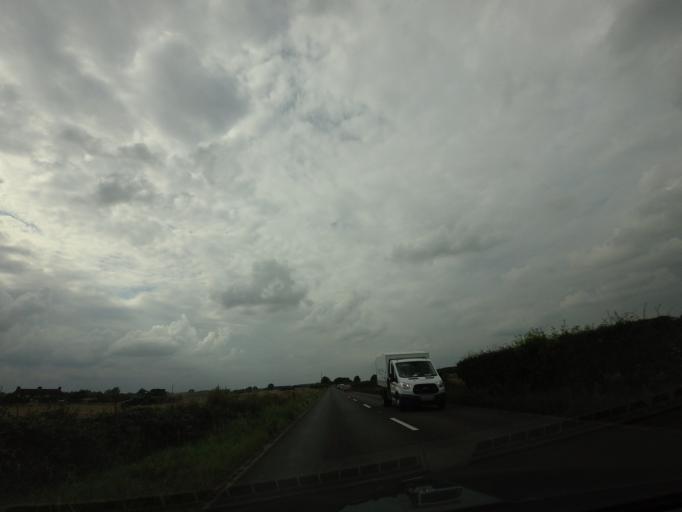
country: GB
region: England
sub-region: Shropshire
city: Tong
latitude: 52.6900
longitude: -2.3152
